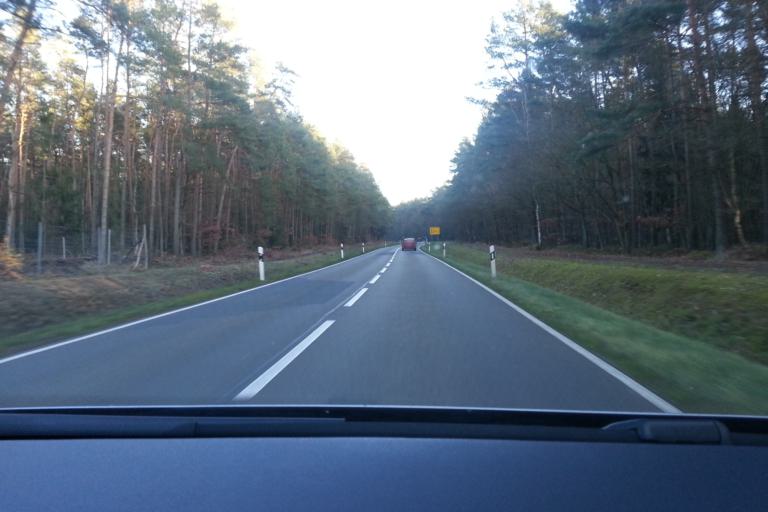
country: DE
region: Mecklenburg-Vorpommern
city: Jatznick
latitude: 53.6380
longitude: 13.9493
